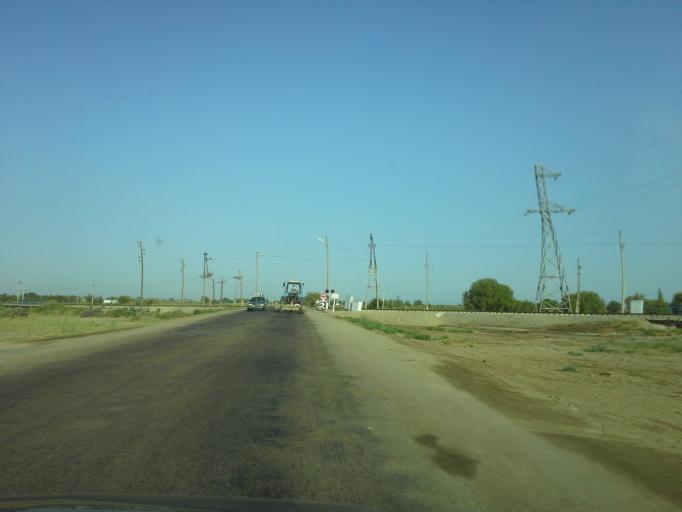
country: UZ
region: Karakalpakstan
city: Khujayli
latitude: 42.2305
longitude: 59.4652
